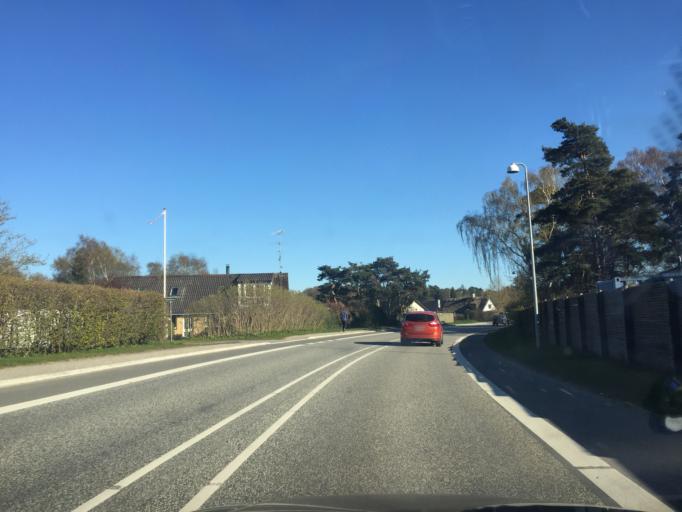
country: DK
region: Capital Region
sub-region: Halsnaes Kommune
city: Frederiksvaerk
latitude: 56.0033
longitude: 12.0111
